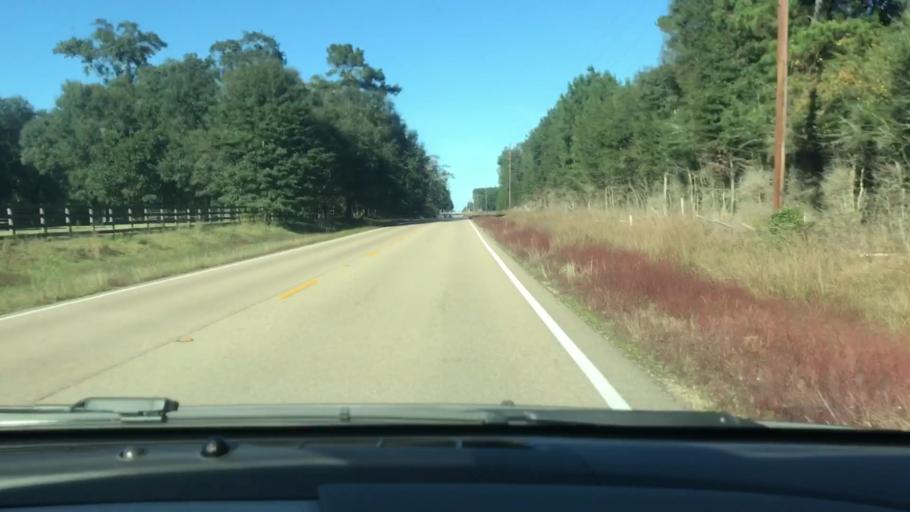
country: US
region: Louisiana
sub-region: Saint Tammany Parish
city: Abita Springs
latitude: 30.5756
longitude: -90.0371
